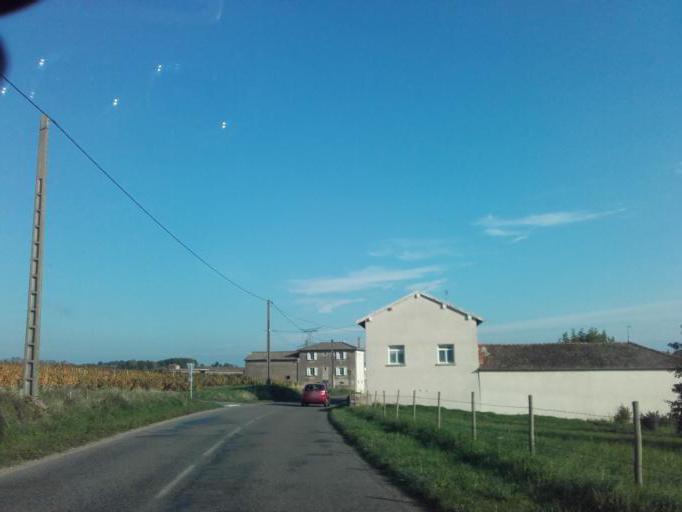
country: FR
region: Bourgogne
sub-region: Departement de Saone-et-Loire
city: La Chapelle-de-Guinchay
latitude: 46.2278
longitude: 4.7285
